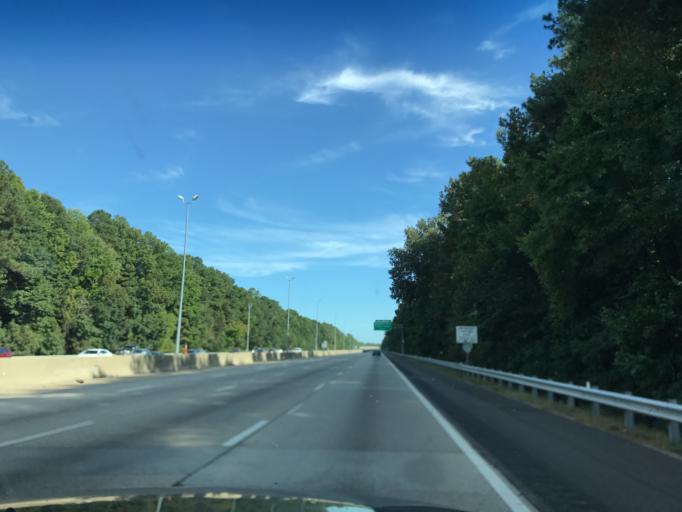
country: US
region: Virginia
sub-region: City of Newport News
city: Newport News
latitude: 37.0725
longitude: -76.4396
